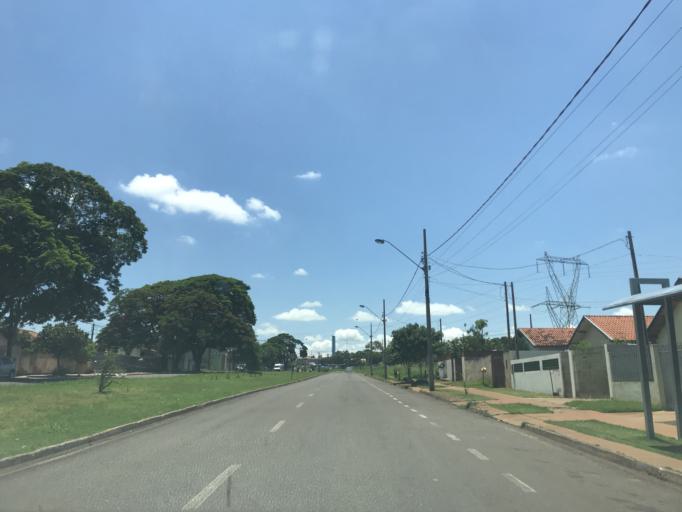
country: BR
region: Parana
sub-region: Maringa
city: Maringa
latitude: -23.4589
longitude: -51.9224
